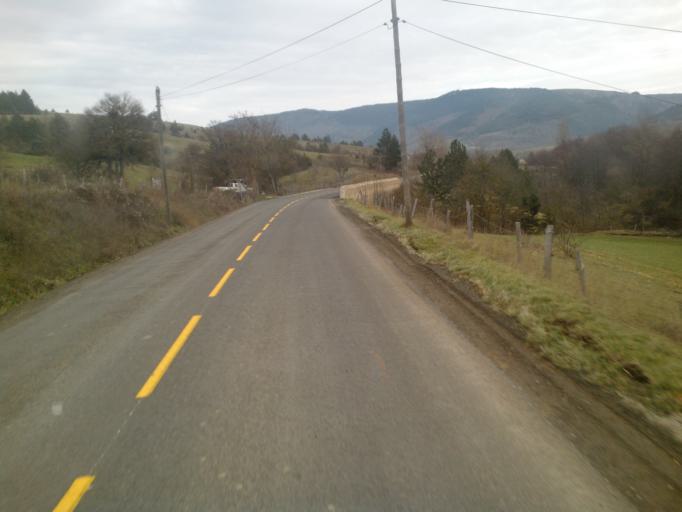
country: FR
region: Languedoc-Roussillon
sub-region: Departement de la Lozere
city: Mende
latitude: 44.4555
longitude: 3.5302
